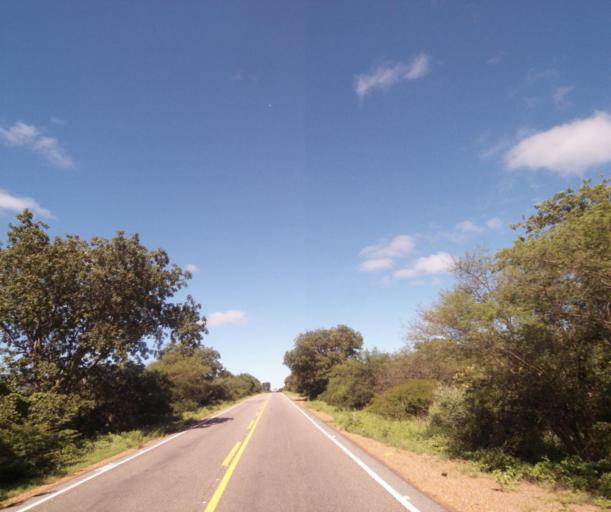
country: BR
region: Bahia
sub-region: Palmas De Monte Alto
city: Palmas de Monte Alto
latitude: -14.2428
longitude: -43.0789
